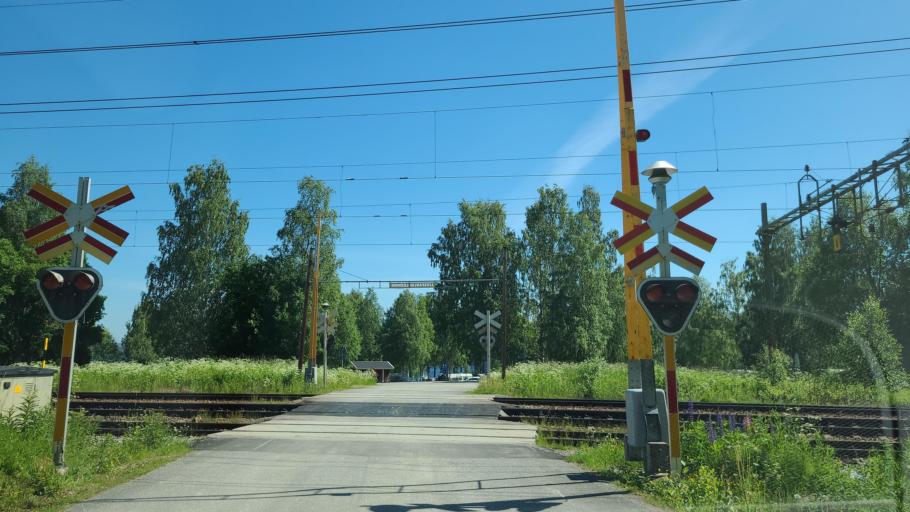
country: SE
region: Vaesterbotten
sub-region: Bjurholms Kommun
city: Bjurholm
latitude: 63.6913
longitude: 18.8646
